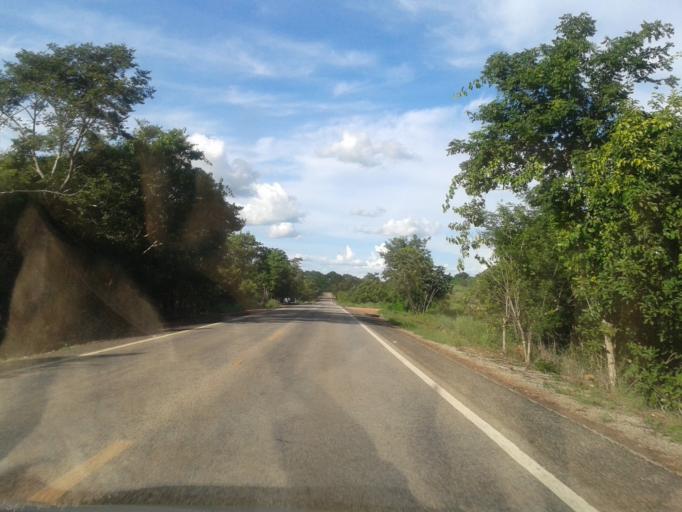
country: BR
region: Goias
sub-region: Mozarlandia
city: Mozarlandia
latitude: -14.5781
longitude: -50.5034
